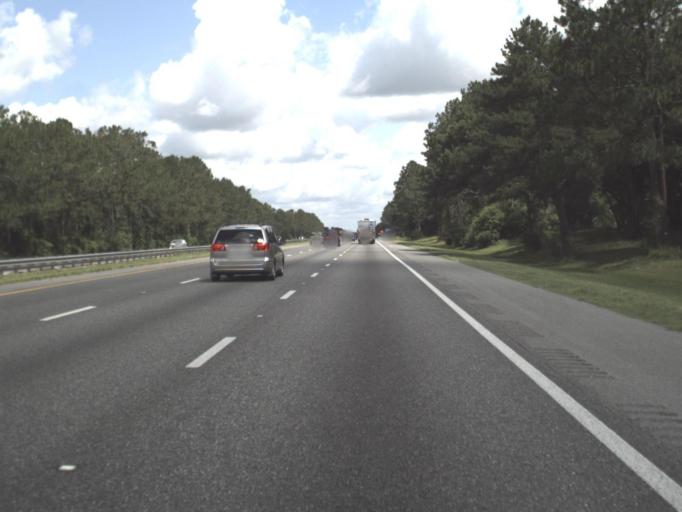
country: US
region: Florida
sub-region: Columbia County
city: Lake City
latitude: 30.0964
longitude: -82.6434
